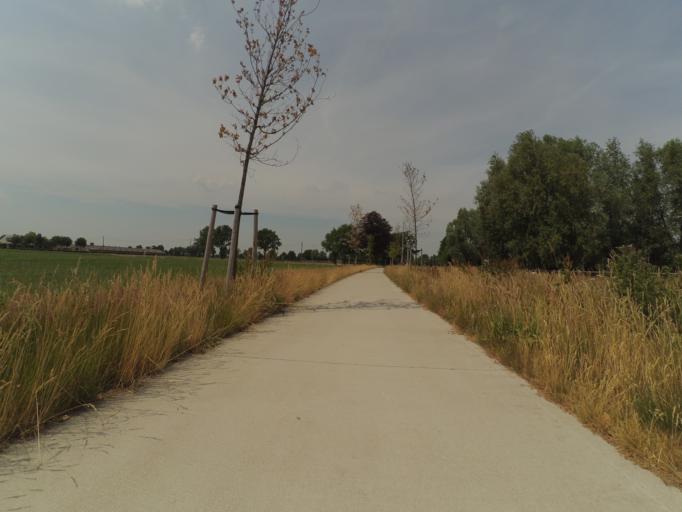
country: BE
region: Flanders
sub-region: Provincie Antwerpen
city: Kalmthout
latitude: 51.4140
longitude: 4.5281
